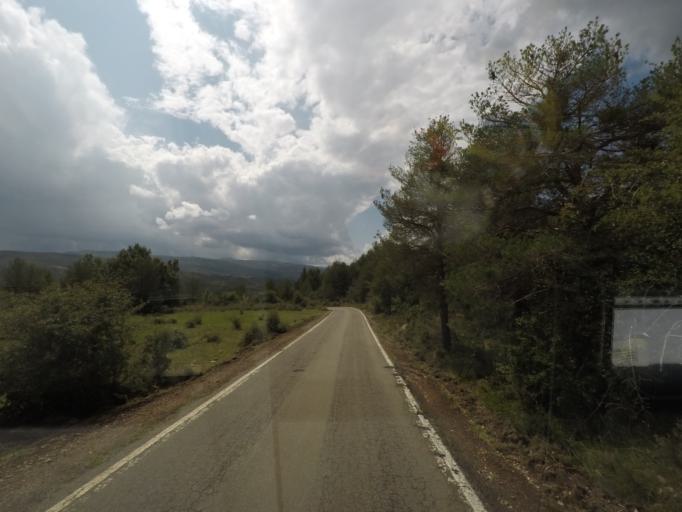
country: ES
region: Aragon
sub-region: Provincia de Huesca
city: Fiscal
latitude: 42.4104
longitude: -0.1311
